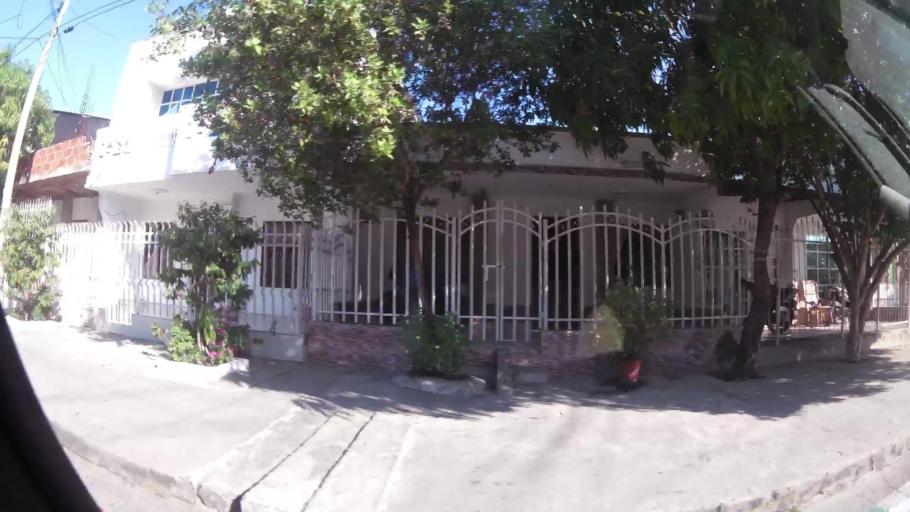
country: CO
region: Bolivar
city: Cartagena
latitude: 10.3914
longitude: -75.5030
